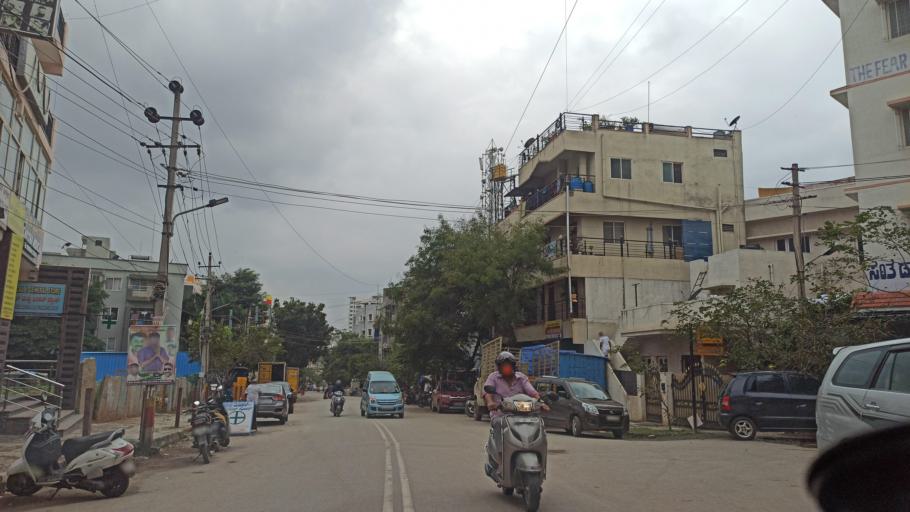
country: IN
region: Karnataka
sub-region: Bangalore Urban
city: Bangalore
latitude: 12.9972
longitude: 77.6873
